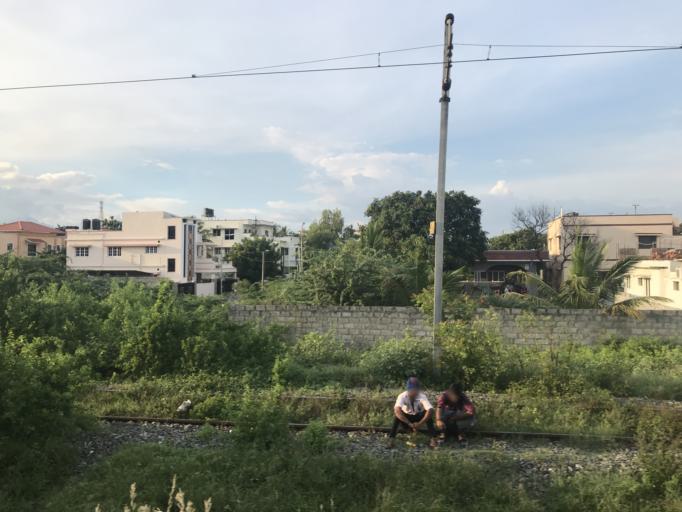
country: IN
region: Tamil Nadu
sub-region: Coimbatore
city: Coimbatore
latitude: 11.0341
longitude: 76.9896
